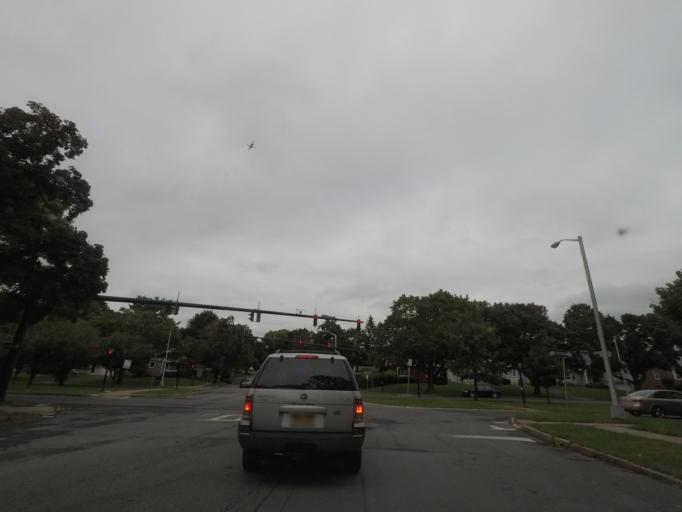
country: US
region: New York
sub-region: Albany County
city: West Albany
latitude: 42.6516
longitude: -73.8023
